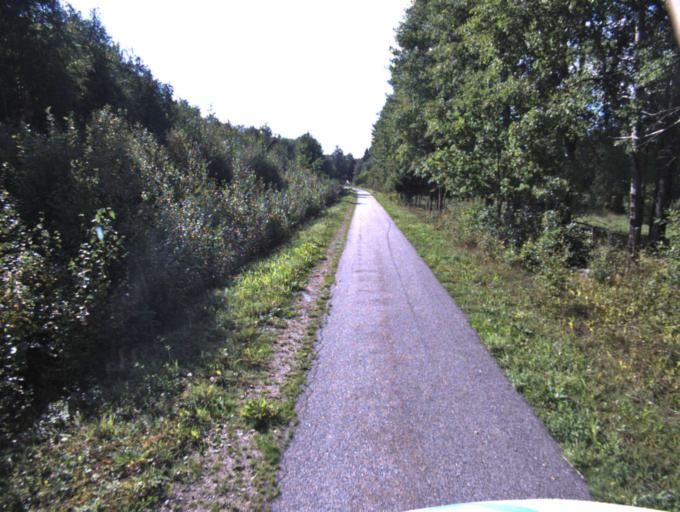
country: SE
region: Vaestra Goetaland
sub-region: Boras Kommun
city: Dalsjofors
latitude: 57.8282
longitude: 13.2023
